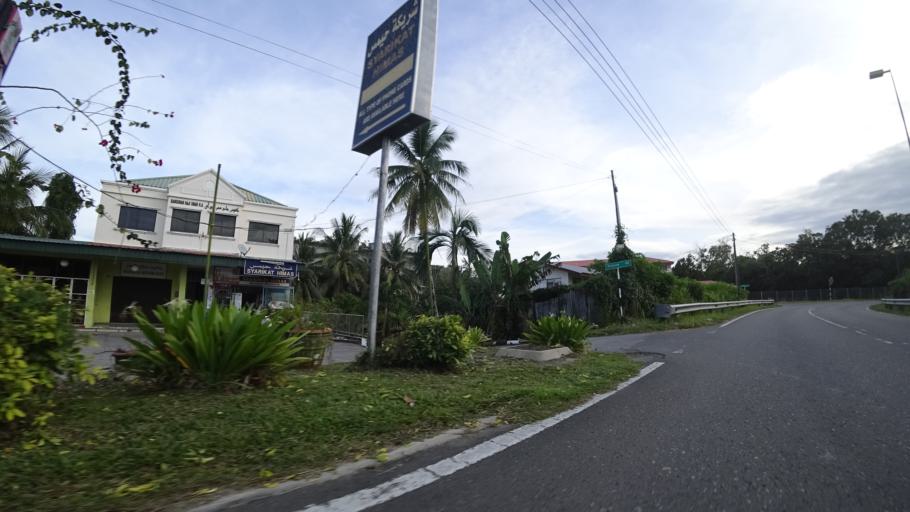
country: BN
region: Brunei and Muara
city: Bandar Seri Begawan
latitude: 4.8847
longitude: 114.9014
